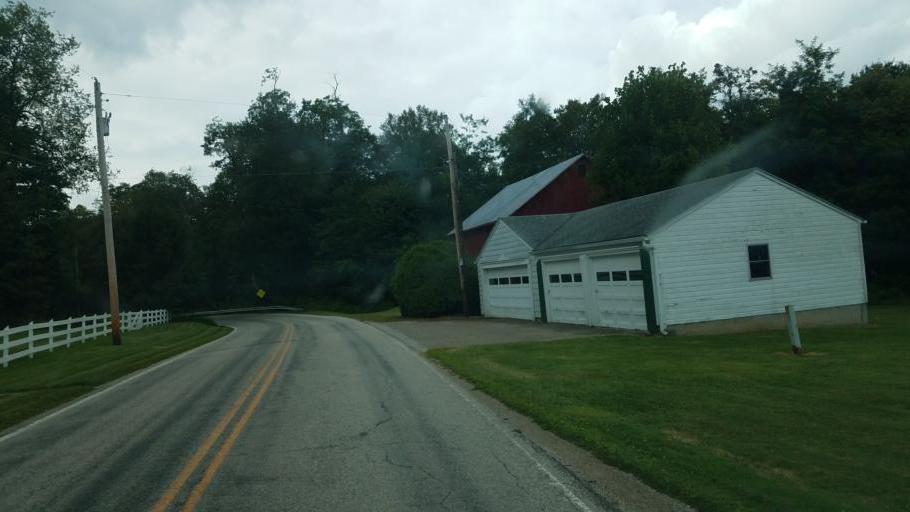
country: US
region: Ohio
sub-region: Sandusky County
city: Bellville
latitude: 40.6279
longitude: -82.4236
